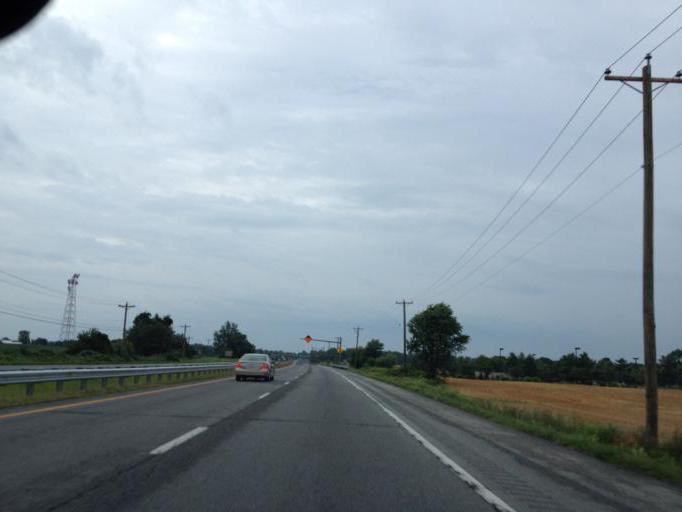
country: US
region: Maryland
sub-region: Queen Anne's County
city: Centreville
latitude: 38.9561
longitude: -76.0860
